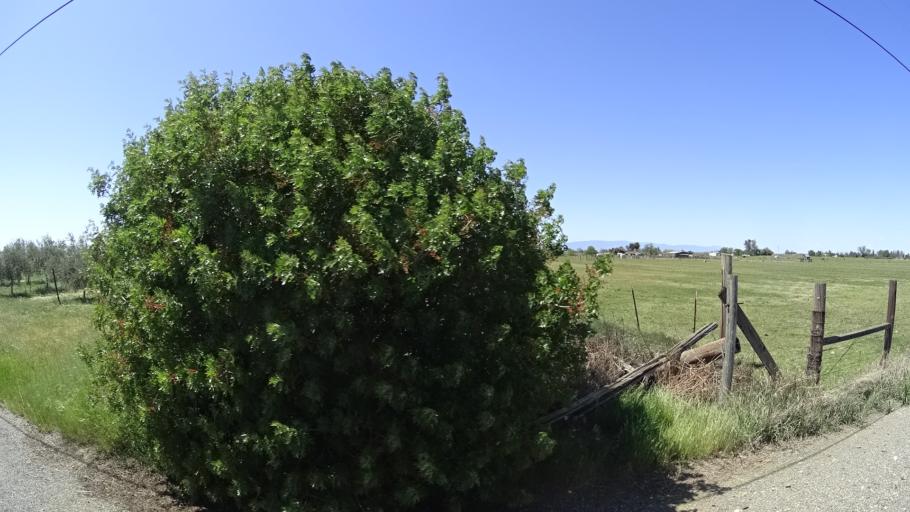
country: US
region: California
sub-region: Glenn County
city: Orland
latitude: 39.7764
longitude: -122.1782
